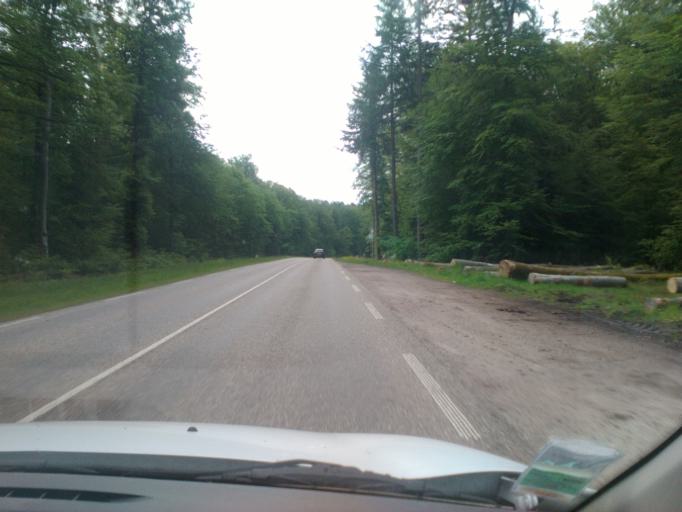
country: FR
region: Lorraine
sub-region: Departement des Vosges
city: Archettes
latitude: 48.1606
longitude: 6.5464
